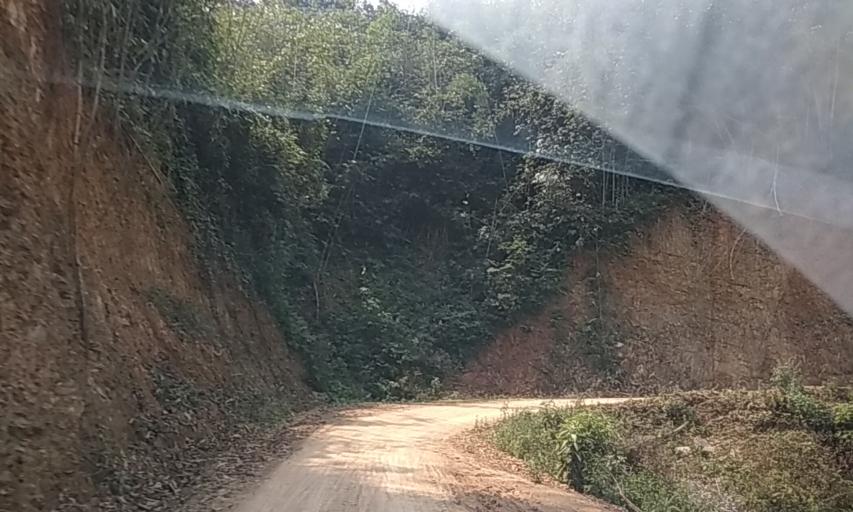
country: LA
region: Phongsali
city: Phongsali
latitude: 21.4643
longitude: 102.4204
